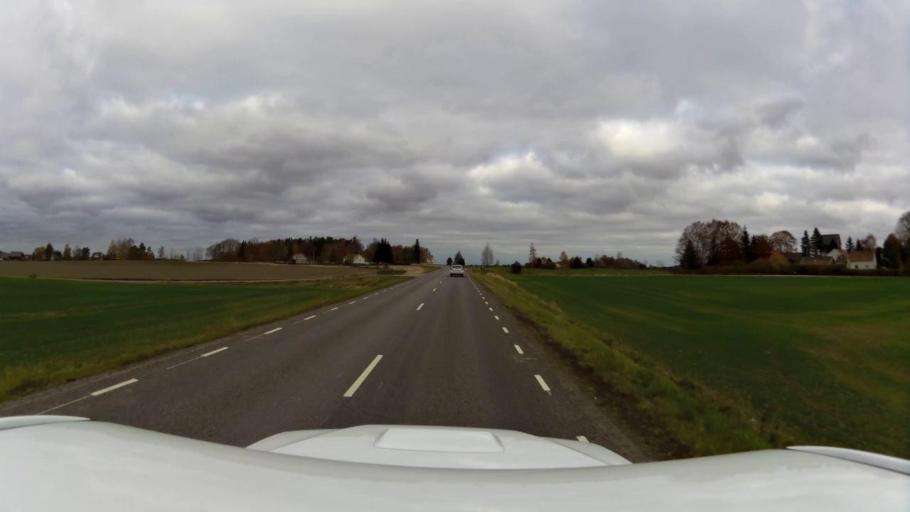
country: SE
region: OEstergoetland
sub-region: Linkopings Kommun
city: Linghem
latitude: 58.4269
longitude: 15.7243
